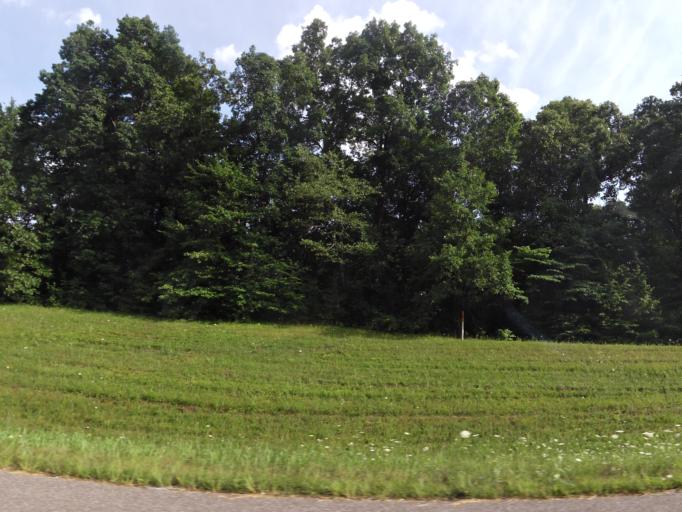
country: US
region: Tennessee
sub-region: Benton County
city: Camden
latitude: 36.0267
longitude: -88.0771
